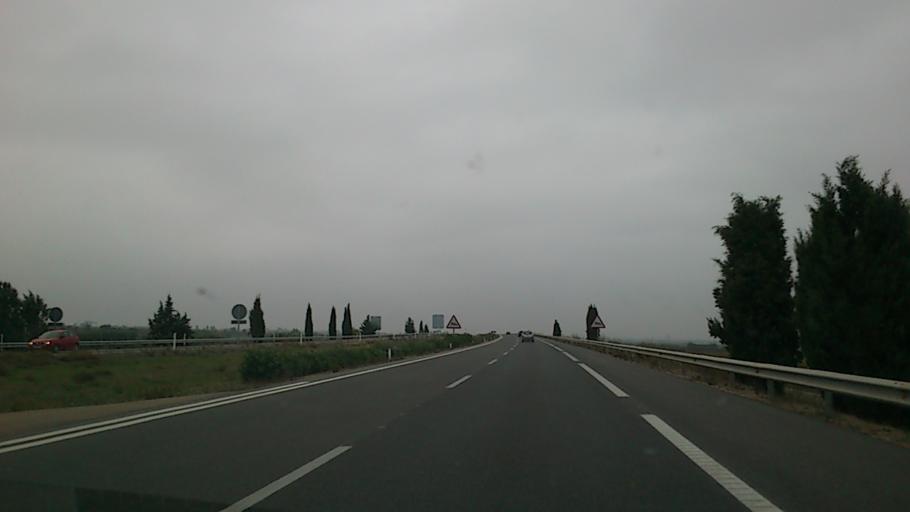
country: ES
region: Aragon
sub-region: Provincia de Zaragoza
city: Alagon
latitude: 41.7776
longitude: -1.1338
